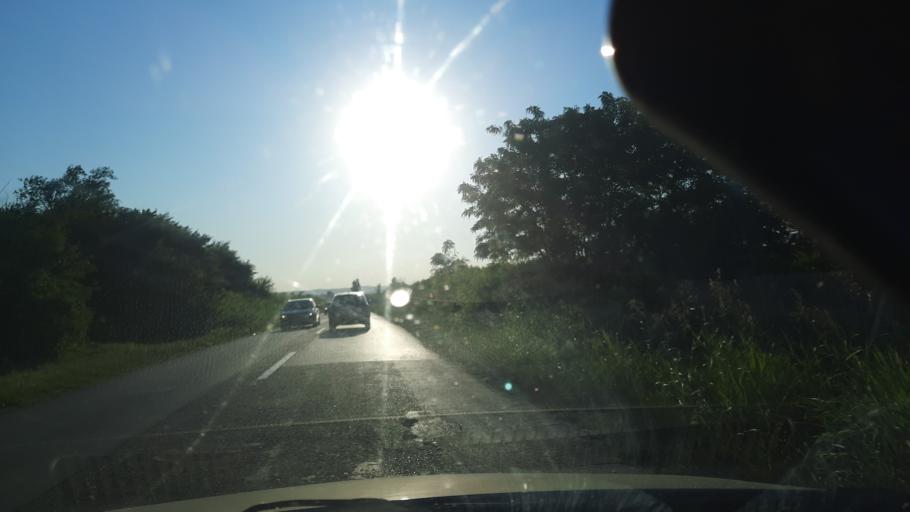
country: RS
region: Central Serbia
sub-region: Branicevski Okrug
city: Malo Crnice
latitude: 44.5796
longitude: 21.3256
